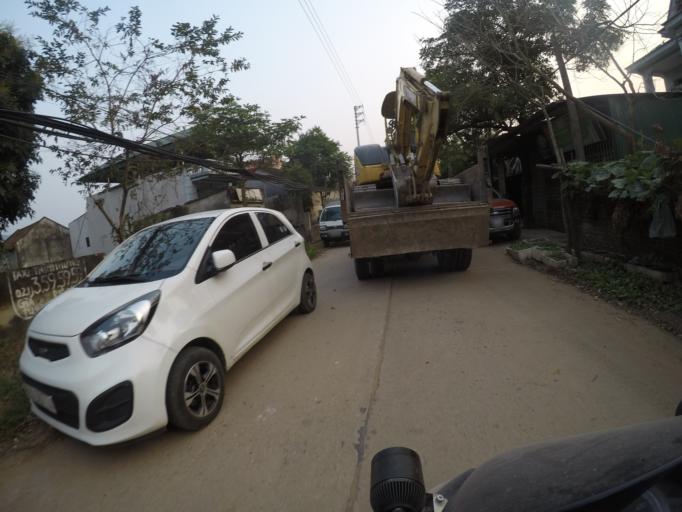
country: VN
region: Vinh Phuc
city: Trai Ngau
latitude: 21.4633
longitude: 105.5703
